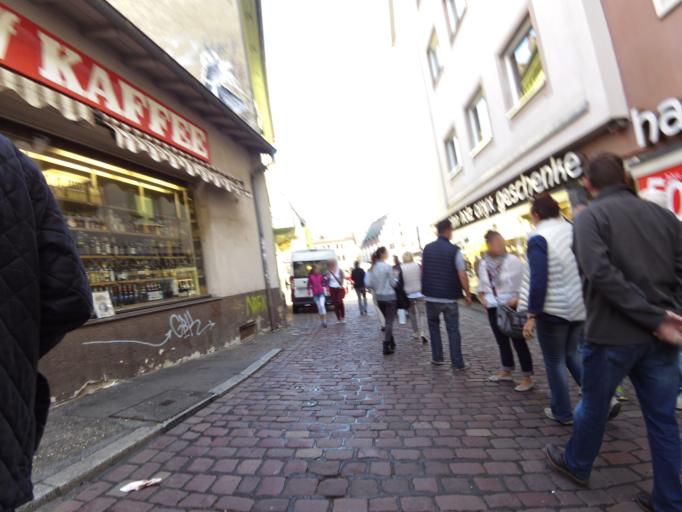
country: DE
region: Baden-Wuerttemberg
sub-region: Freiburg Region
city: Freiburg
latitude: 47.9956
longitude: 7.8512
